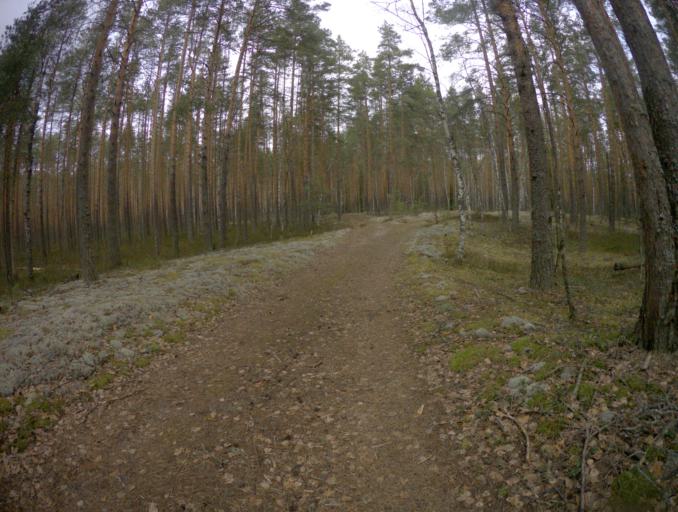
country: RU
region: Vladimir
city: Raduzhnyy
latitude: 55.9472
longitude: 40.2774
